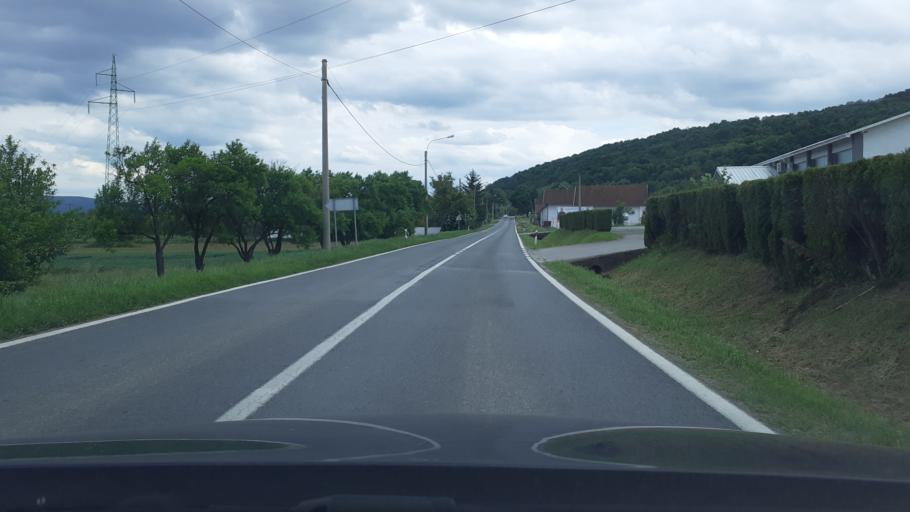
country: HR
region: Pozesko-Slavonska
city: Jaksic
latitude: 45.3194
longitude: 17.7723
